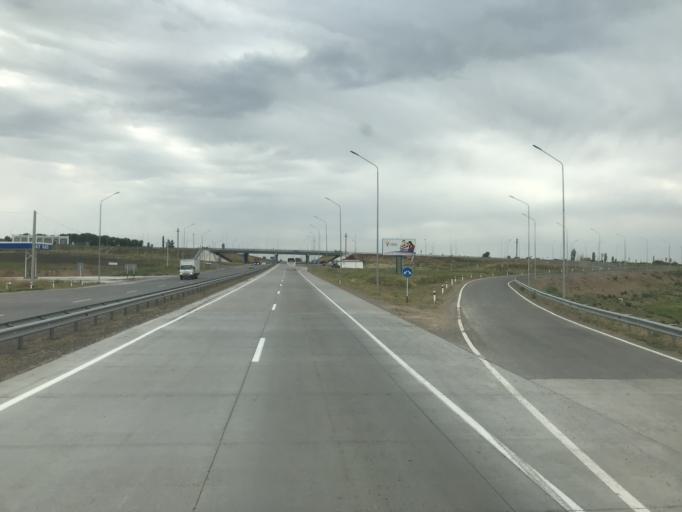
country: UZ
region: Toshkent
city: Salor
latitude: 41.5013
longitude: 69.3596
